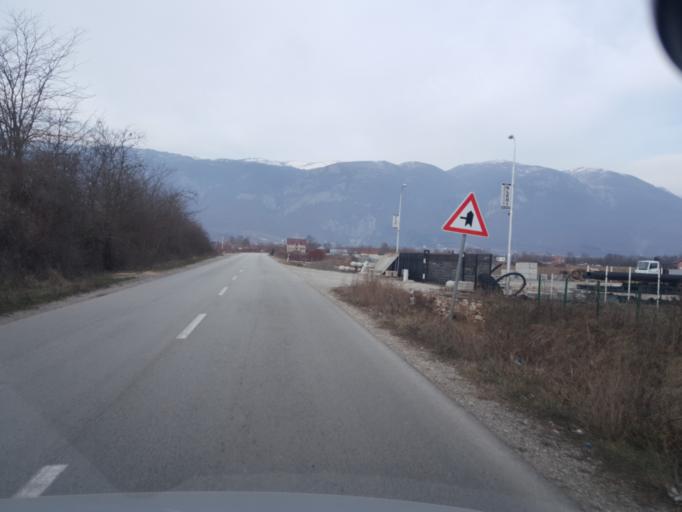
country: XK
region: Pec
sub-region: Komuna e Istogut
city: Istok
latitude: 42.7470
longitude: 20.4868
